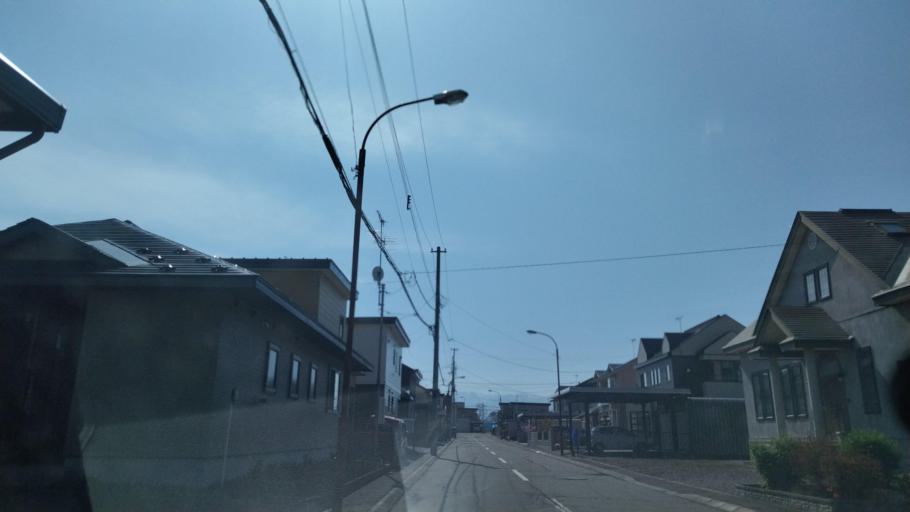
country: JP
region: Hokkaido
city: Obihiro
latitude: 42.9174
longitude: 143.0577
